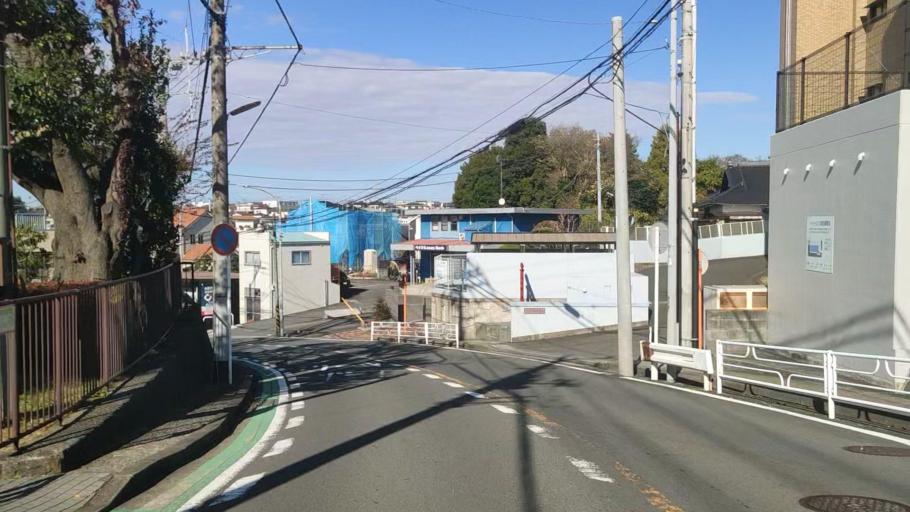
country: JP
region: Kanagawa
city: Minami-rinkan
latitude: 35.4593
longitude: 139.5305
